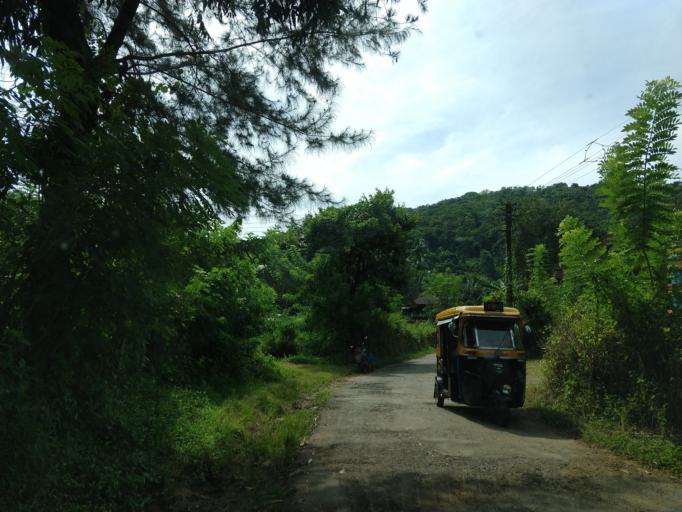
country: IN
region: Maharashtra
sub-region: Sindhudurg
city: Savantvadi
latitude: 15.9724
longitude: 73.7878
